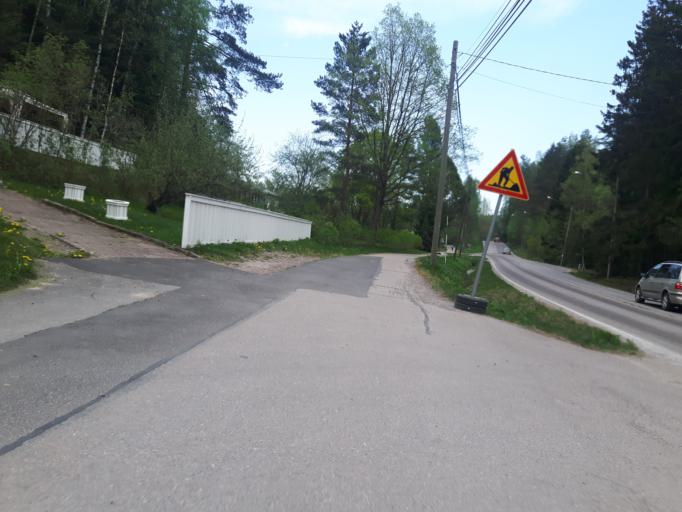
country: FI
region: Uusimaa
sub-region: Porvoo
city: Porvoo
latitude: 60.4016
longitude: 25.7222
